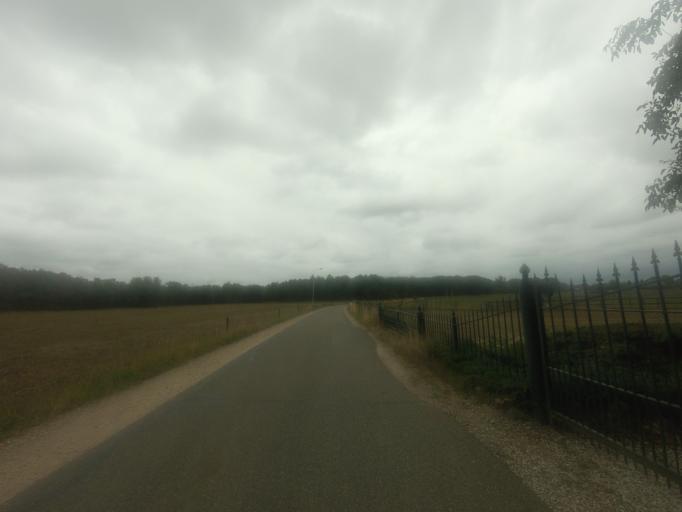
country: NL
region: North Brabant
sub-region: Gemeente Grave
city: Grave
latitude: 51.7906
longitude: 5.7634
